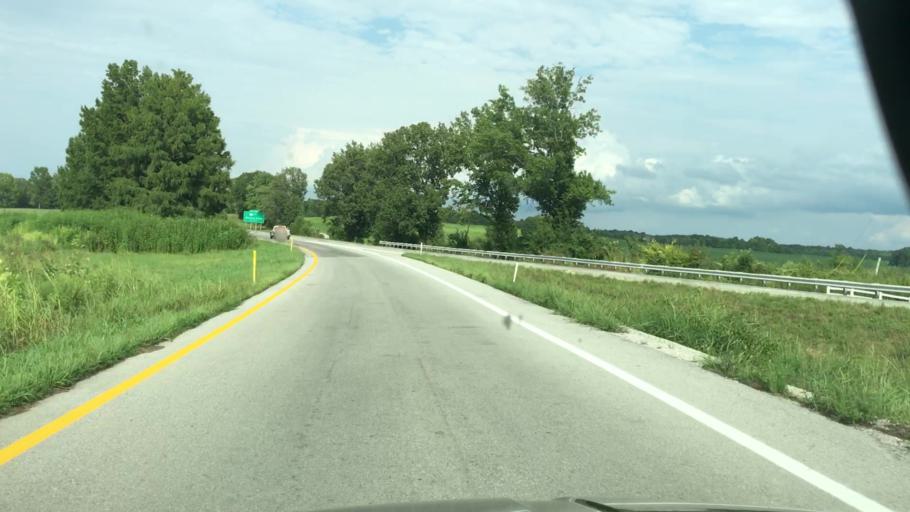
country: US
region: Kentucky
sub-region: Ohio County
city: Beaver Dam
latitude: 37.3772
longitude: -86.8241
